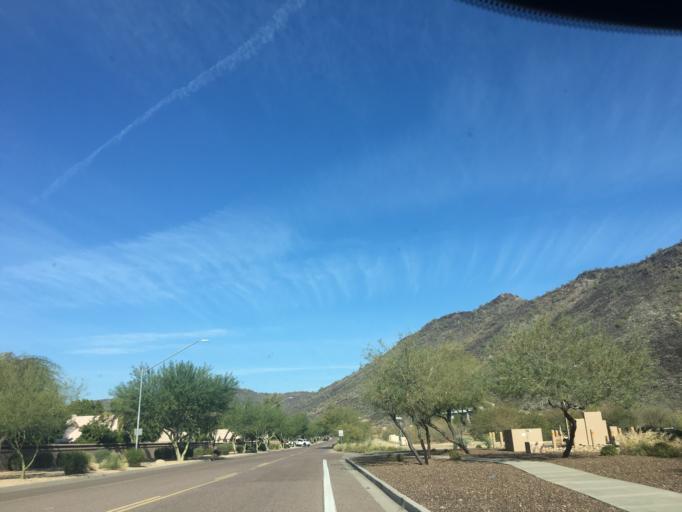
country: US
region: Arizona
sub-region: Maricopa County
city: Peoria
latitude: 33.6702
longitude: -112.1693
